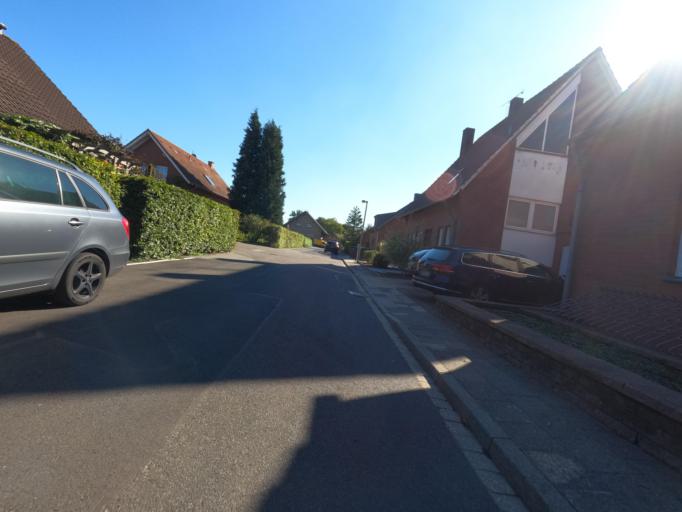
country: DE
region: North Rhine-Westphalia
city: Huckelhoven
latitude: 51.0448
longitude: 6.2498
